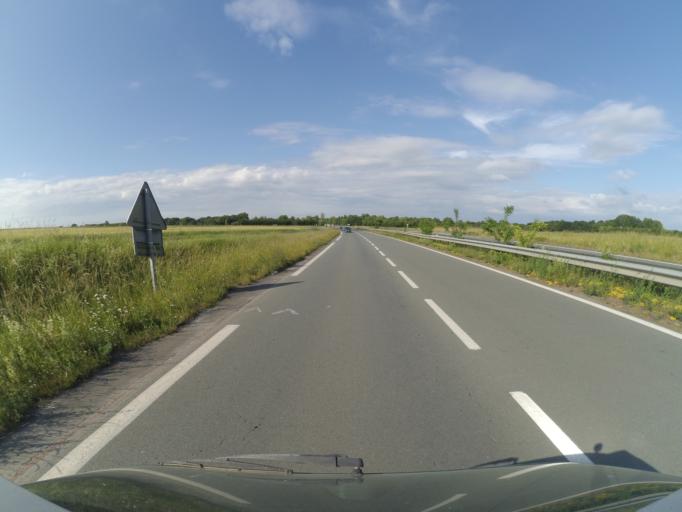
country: FR
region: Poitou-Charentes
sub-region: Departement de la Charente-Maritime
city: Saint-Agnant
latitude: 45.8794
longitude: -0.9644
